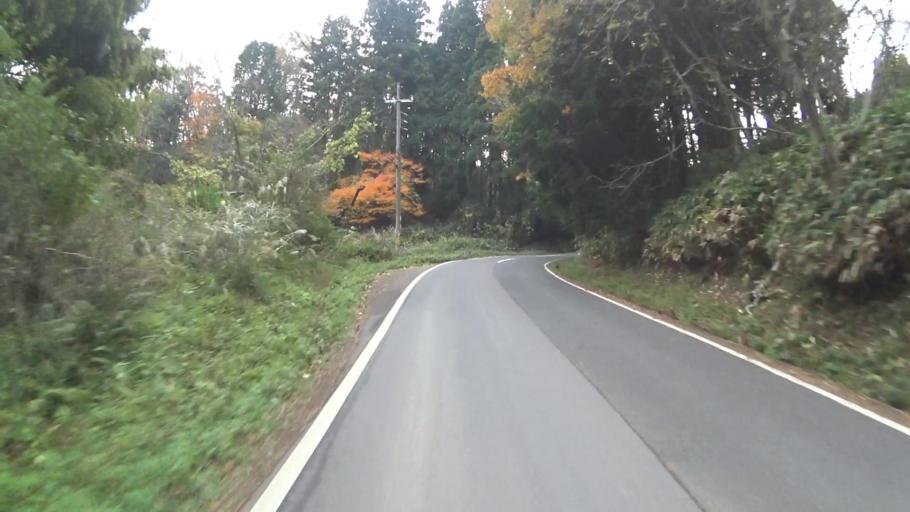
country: JP
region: Kyoto
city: Maizuru
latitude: 35.5419
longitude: 135.4508
